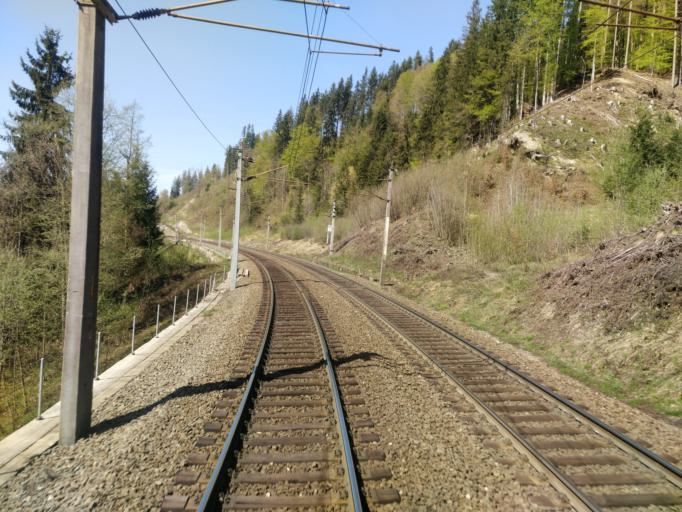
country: AT
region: Tyrol
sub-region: Politischer Bezirk Kitzbuhel
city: Westendorf
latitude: 47.4261
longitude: 12.1873
